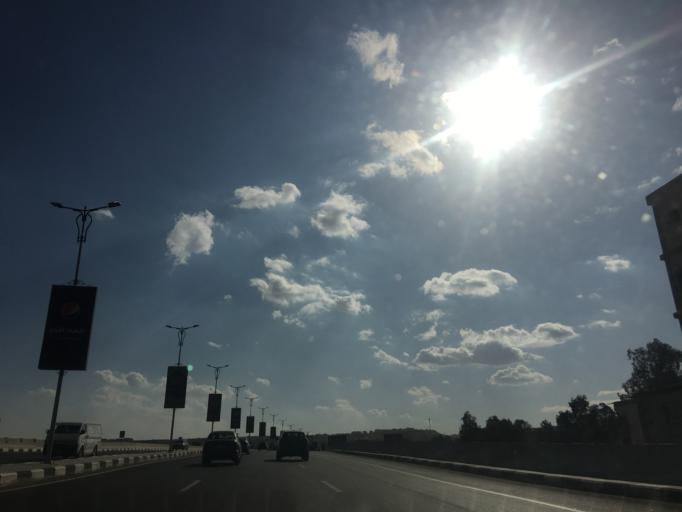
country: EG
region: Muhafazat al Qahirah
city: Cairo
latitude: 30.0440
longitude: 31.3080
